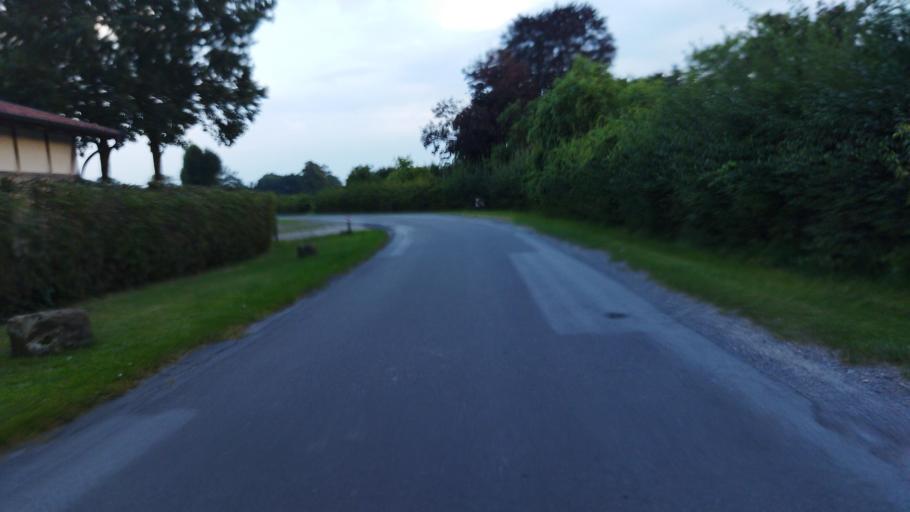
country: DE
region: Lower Saxony
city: Bad Iburg
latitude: 52.1345
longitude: 8.0546
